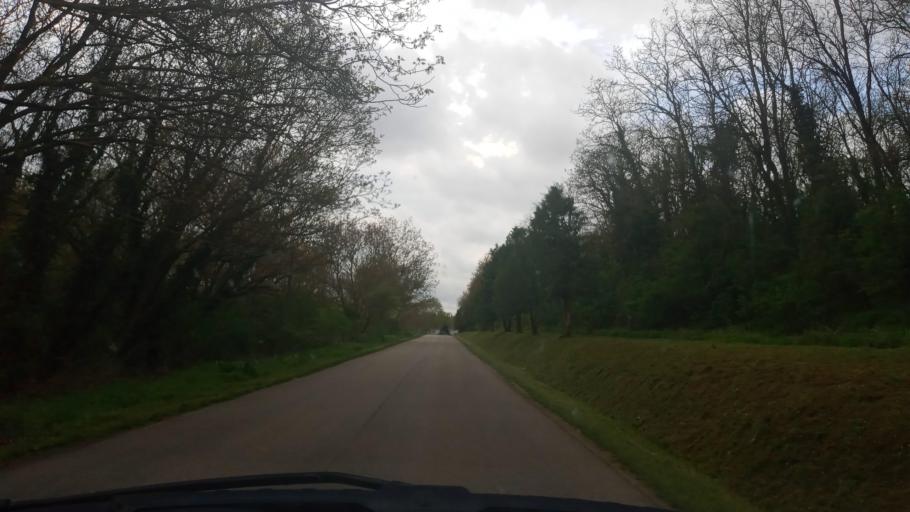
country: HU
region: Baranya
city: Boly
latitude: 45.9897
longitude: 18.4189
